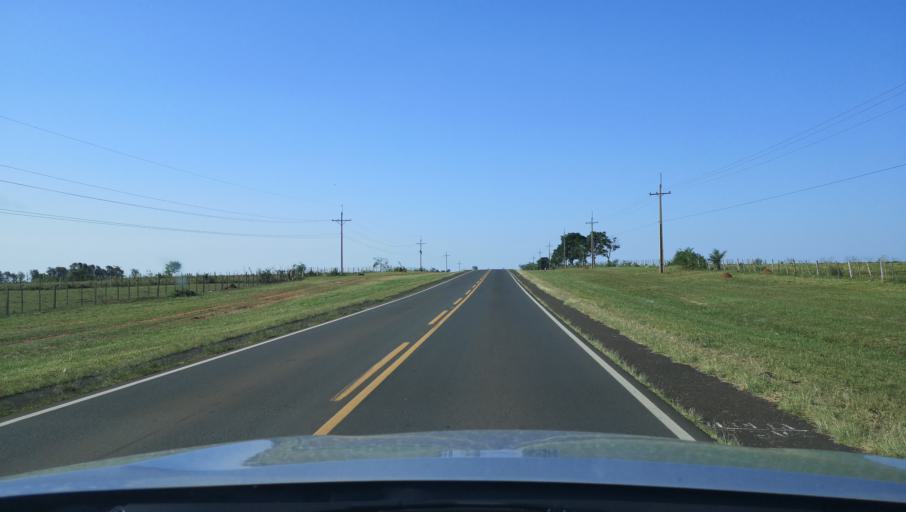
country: PY
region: Misiones
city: Santa Maria
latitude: -26.8145
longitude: -57.0234
